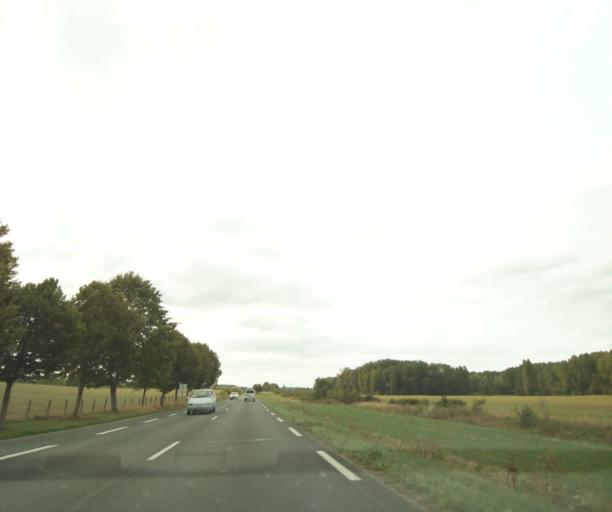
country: FR
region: Centre
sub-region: Departement d'Indre-et-Loire
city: Perrusson
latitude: 47.0788
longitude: 1.0495
